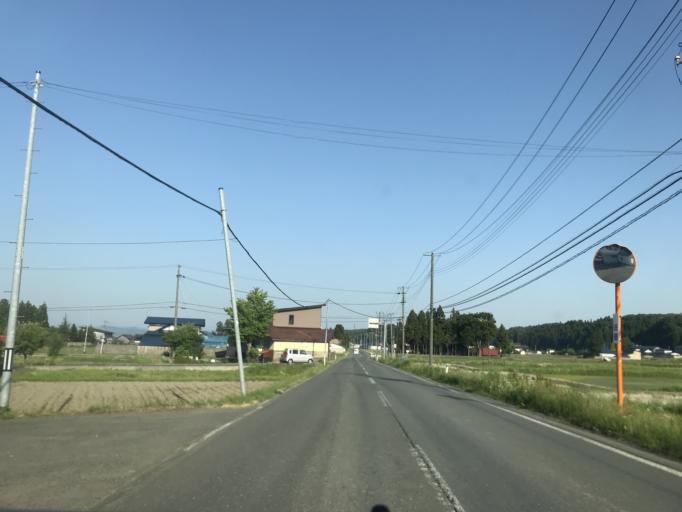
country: JP
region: Iwate
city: Kitakami
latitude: 39.2881
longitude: 141.0018
